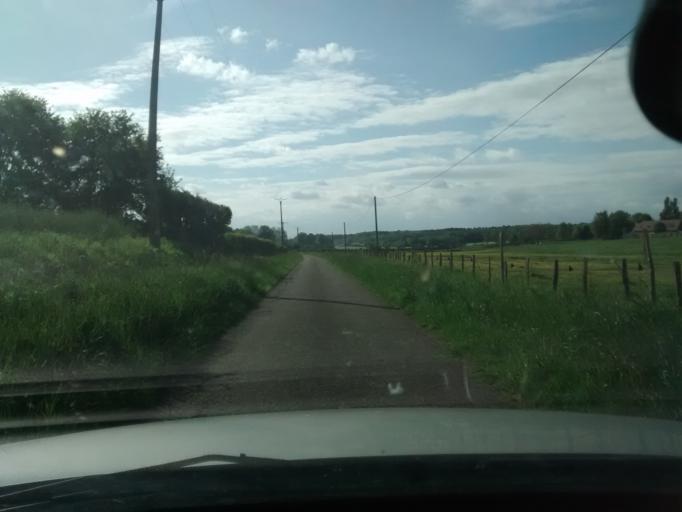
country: FR
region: Pays de la Loire
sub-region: Departement de la Sarthe
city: Challes
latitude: 47.9529
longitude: 0.4579
